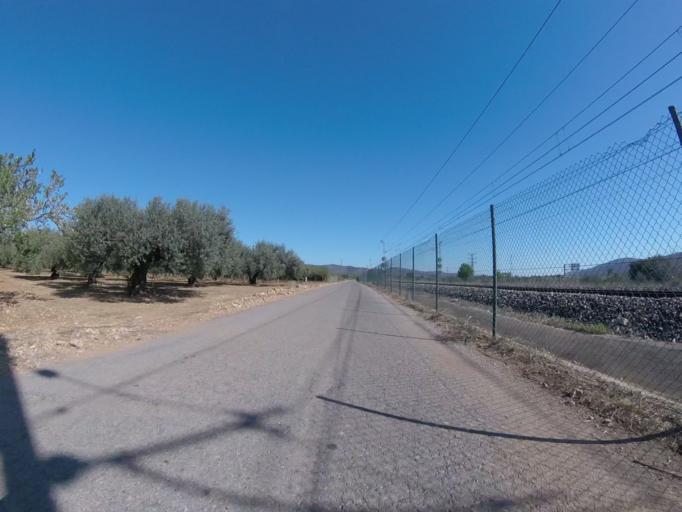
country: ES
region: Valencia
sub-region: Provincia de Castello
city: Alcala de Xivert
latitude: 40.3147
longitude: 0.2327
